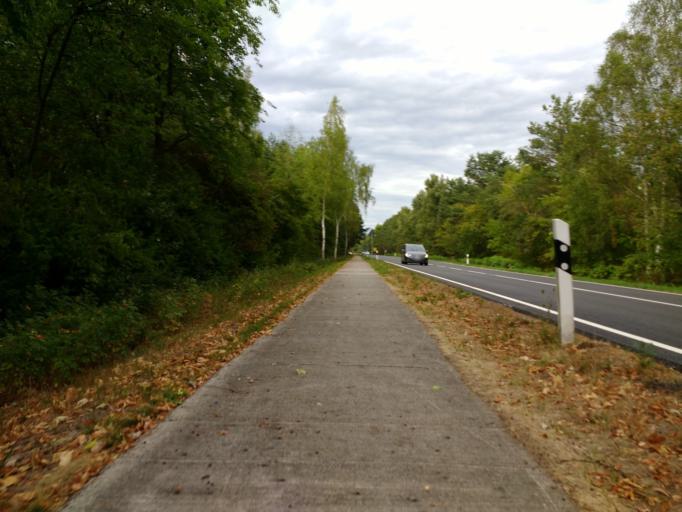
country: DE
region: Lower Saxony
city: Gifhorn
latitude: 52.4691
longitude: 10.5766
